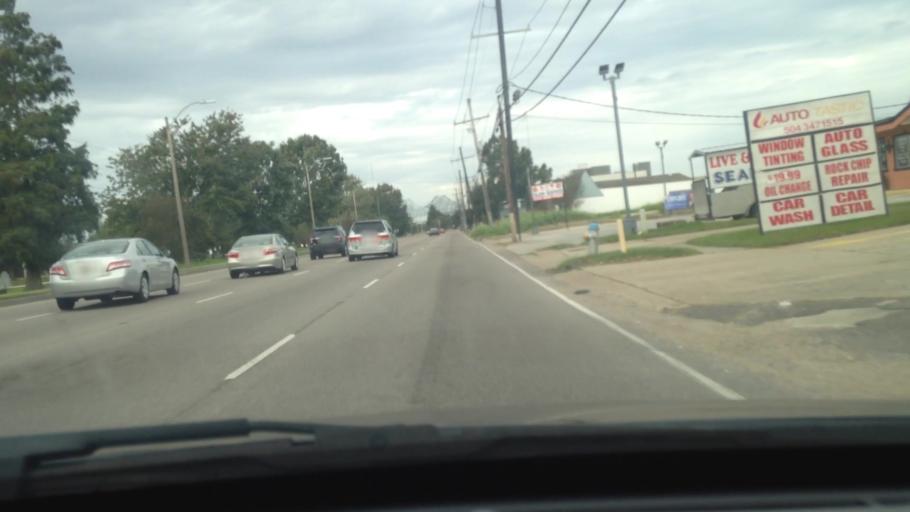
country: US
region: Louisiana
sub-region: Jefferson Parish
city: Terrytown
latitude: 29.9269
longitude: -90.0251
